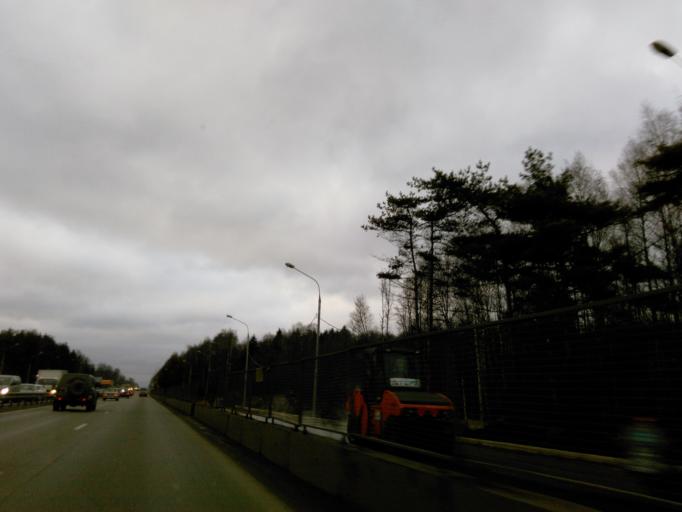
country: RU
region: Moskovskaya
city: Mendeleyevo
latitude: 56.0169
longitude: 37.2012
